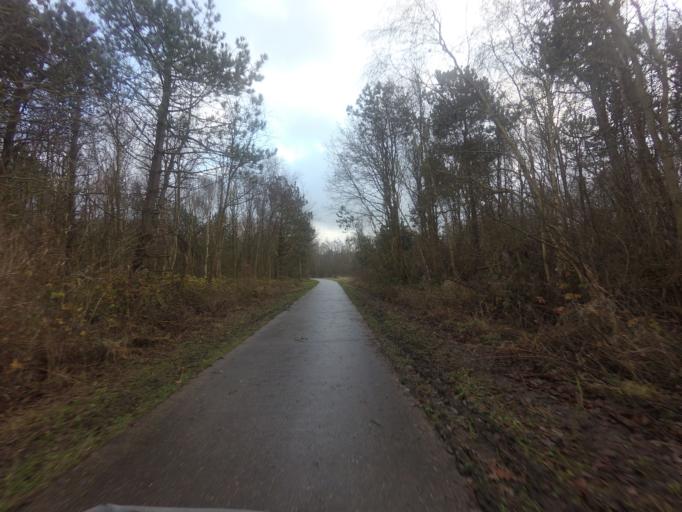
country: NL
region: North Holland
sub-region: Gemeente Texel
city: Den Burg
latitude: 53.1660
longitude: 4.8472
